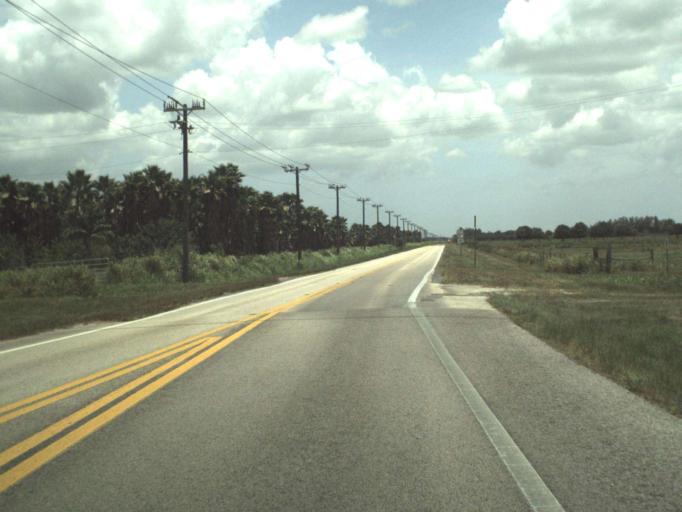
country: US
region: Florida
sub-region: Saint Lucie County
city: Fort Pierce South
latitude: 27.3744
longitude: -80.4813
